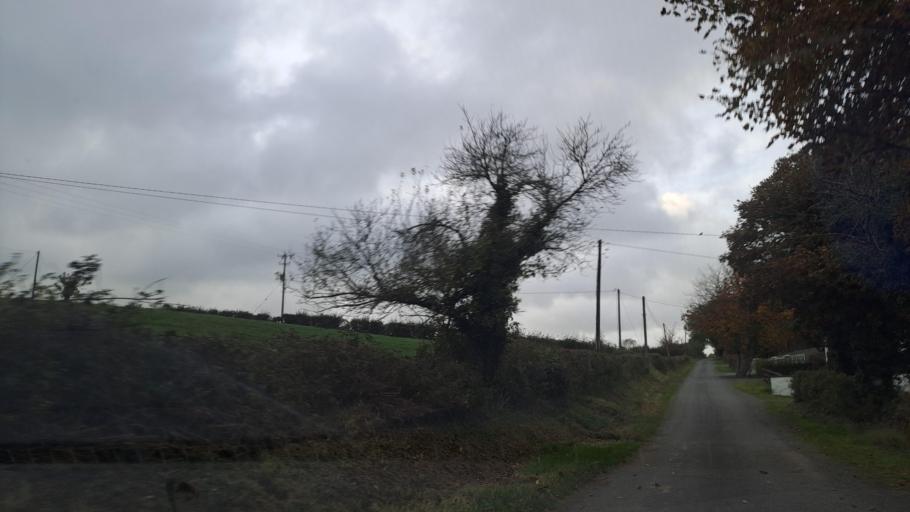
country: IE
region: Ulster
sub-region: County Monaghan
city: Carrickmacross
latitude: 54.0129
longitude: -6.7529
